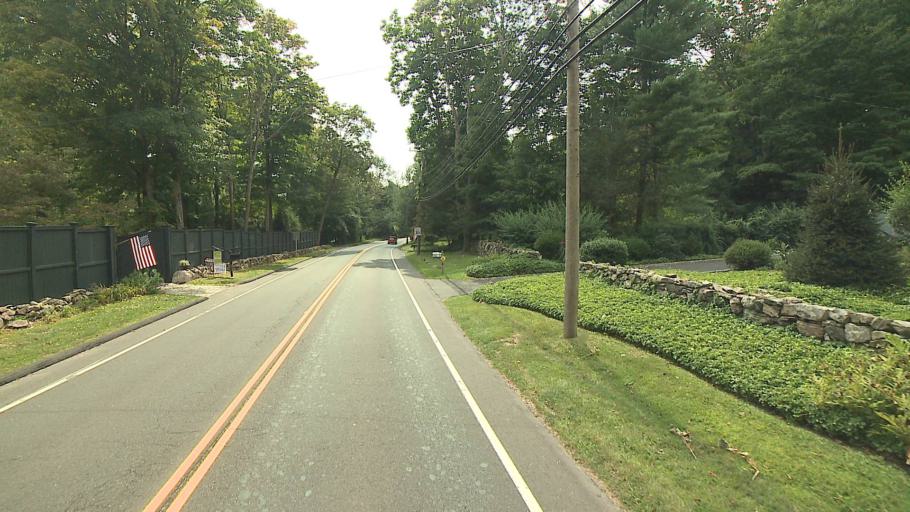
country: US
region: Connecticut
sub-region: Fairfield County
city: Ridgefield
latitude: 41.2987
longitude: -73.5053
